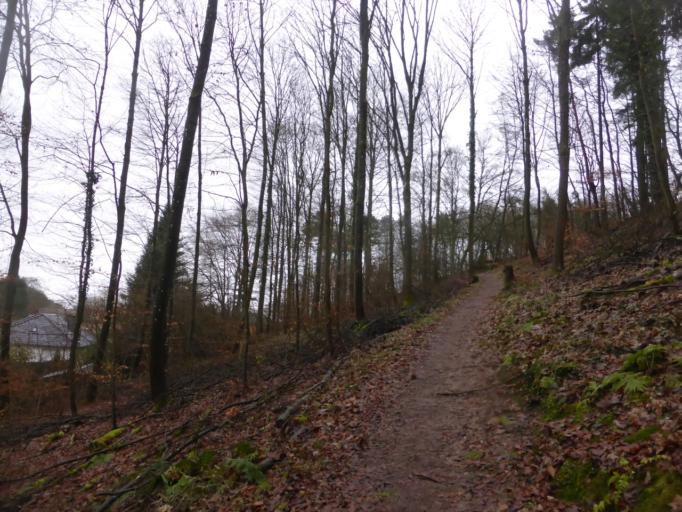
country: LU
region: Luxembourg
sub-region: Canton de Mersch
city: Lorentzweiler
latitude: 49.7021
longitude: 6.1620
